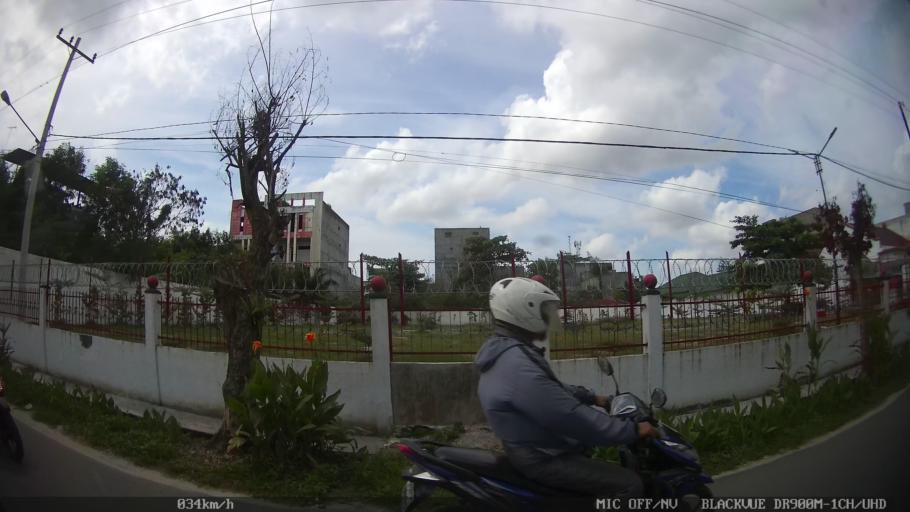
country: ID
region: North Sumatra
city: Percut
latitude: 3.5630
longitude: 98.8718
